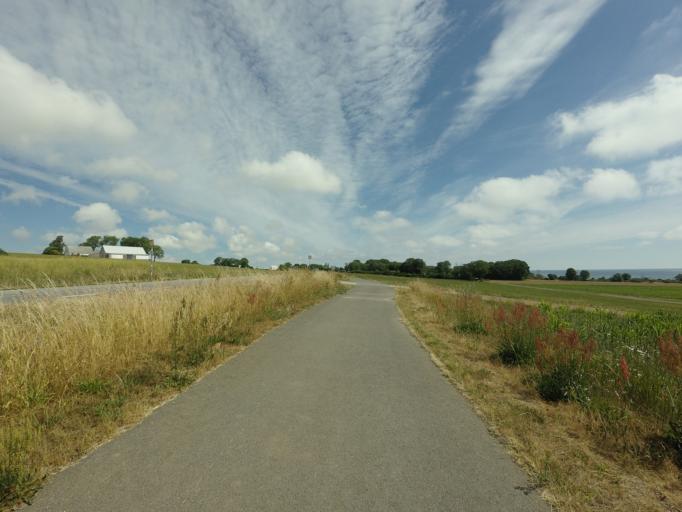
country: SE
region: Skane
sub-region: Simrishamns Kommun
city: Simrishamn
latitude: 55.4938
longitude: 14.3139
